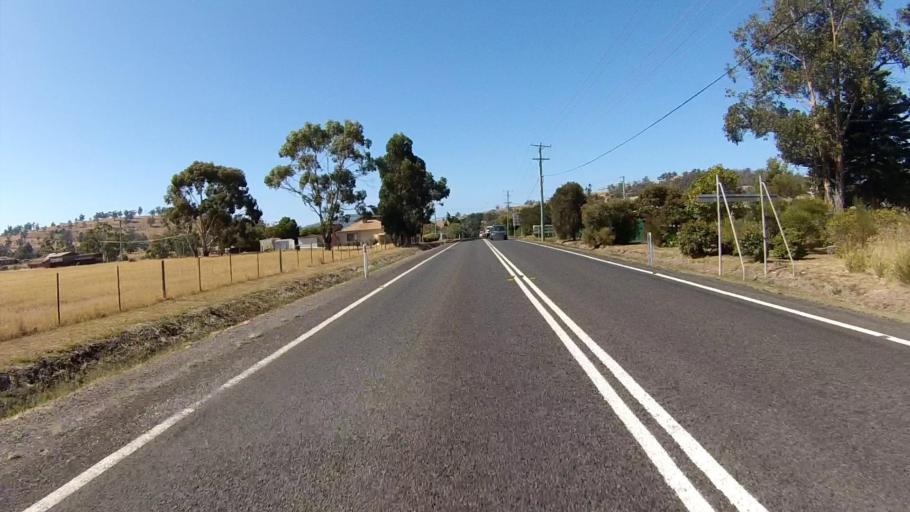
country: AU
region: Tasmania
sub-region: Sorell
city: Sorell
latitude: -42.5013
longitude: 147.9160
